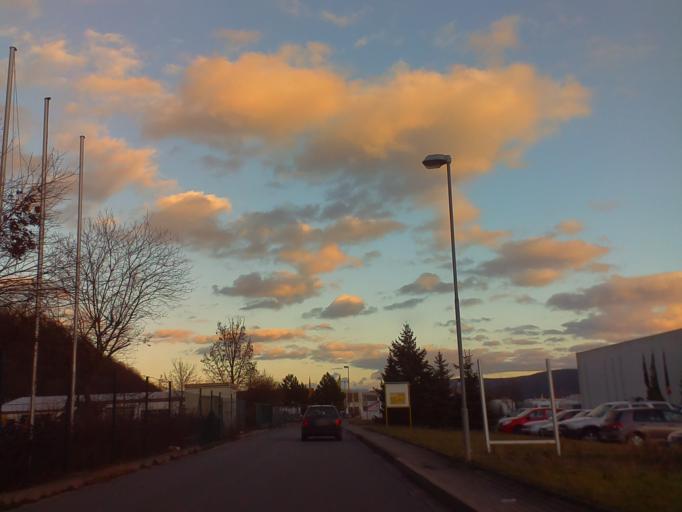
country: DE
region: Thuringia
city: Rudolstadt
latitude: 50.7279
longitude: 11.3797
